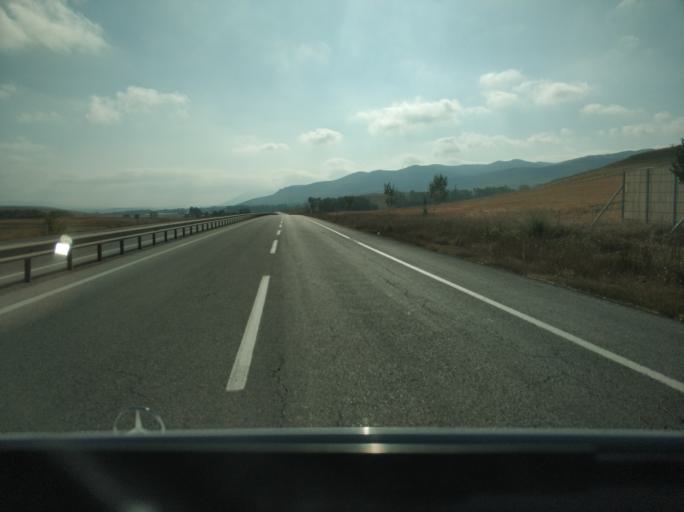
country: TR
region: Sivas
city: Yildizeli
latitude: 39.8355
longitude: 36.4364
